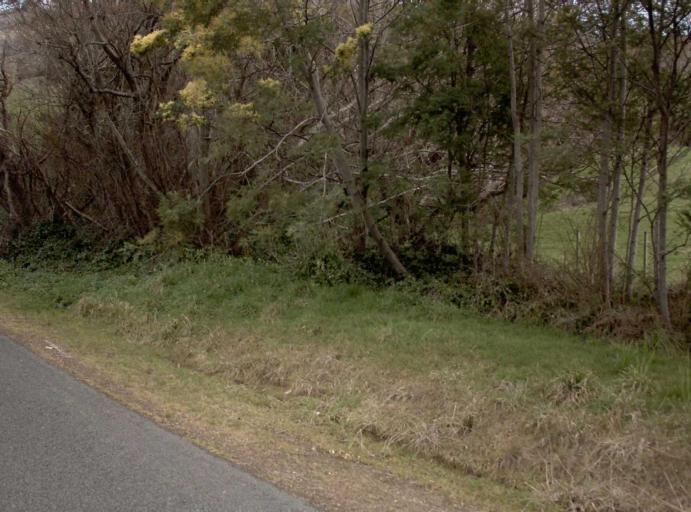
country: AU
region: Tasmania
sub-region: Launceston
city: Mayfield
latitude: -41.2063
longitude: 147.1177
